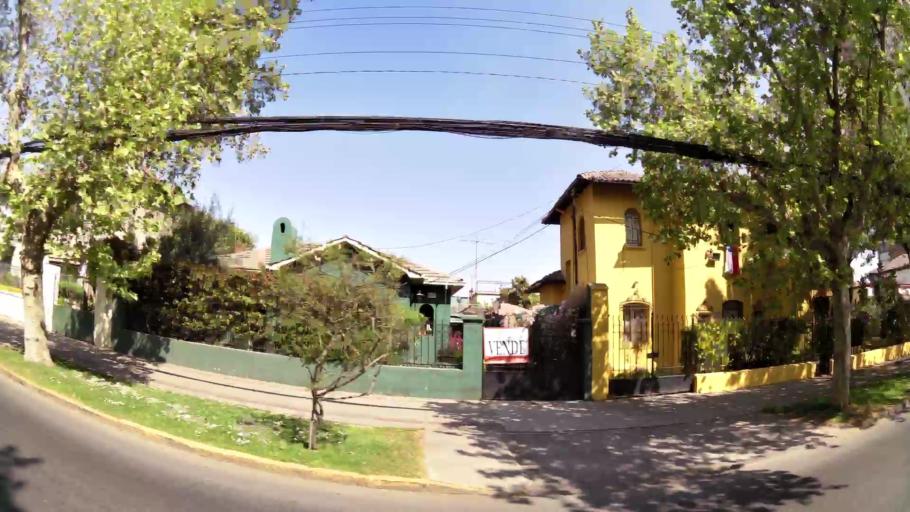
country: CL
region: Santiago Metropolitan
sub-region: Provincia de Santiago
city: Santiago
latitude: -33.4555
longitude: -70.6222
